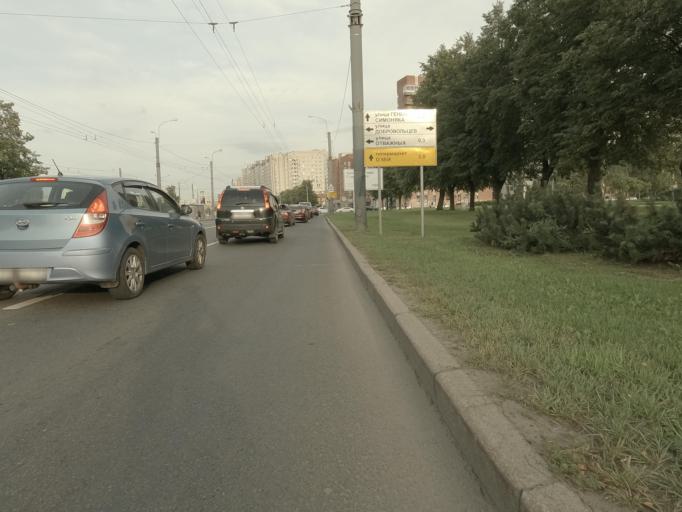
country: RU
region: St.-Petersburg
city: Uritsk
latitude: 59.8334
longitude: 30.1634
